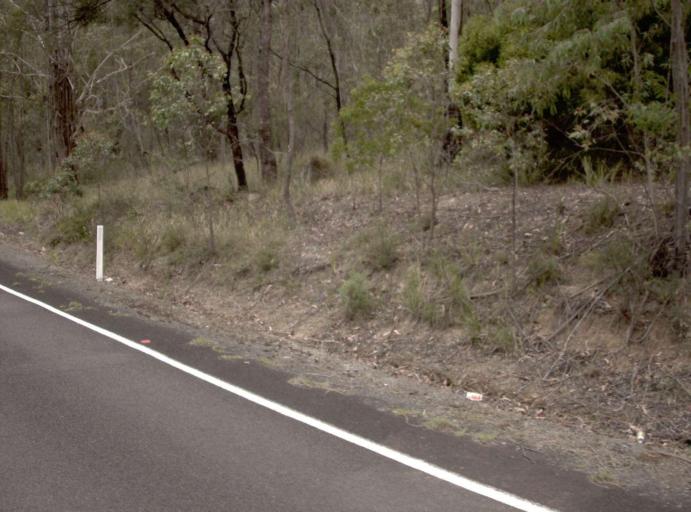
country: AU
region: New South Wales
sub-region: Bombala
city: Bombala
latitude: -37.2774
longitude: 149.2242
